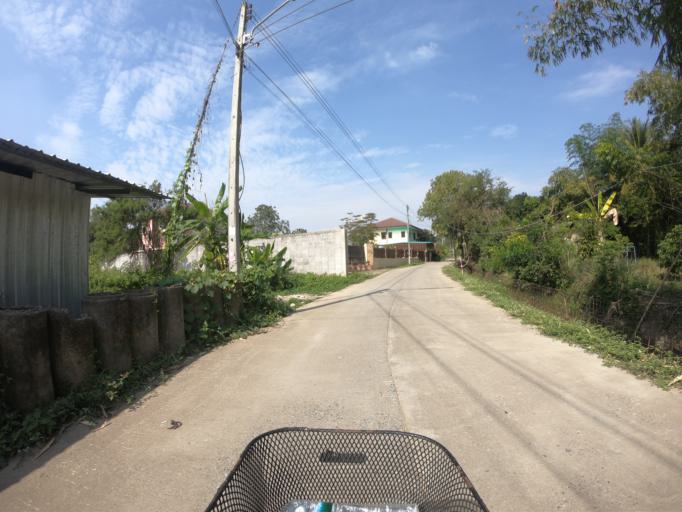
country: TH
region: Chiang Mai
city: Saraphi
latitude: 18.7062
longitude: 99.0501
